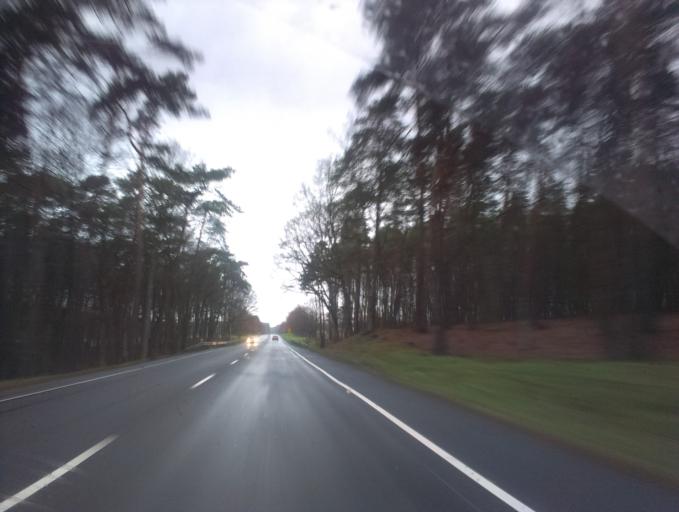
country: PL
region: Greater Poland Voivodeship
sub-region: Powiat chodzieski
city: Chodziez
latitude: 53.0068
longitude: 16.8565
